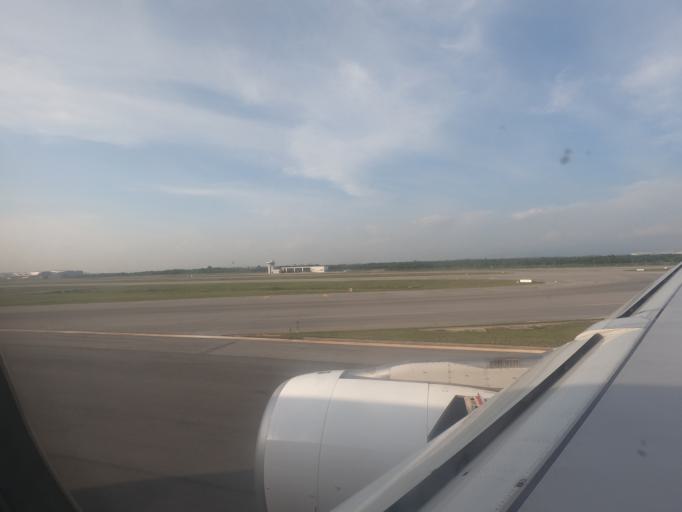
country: MY
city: Sungai Pelek New Village
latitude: 2.7209
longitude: 101.6891
